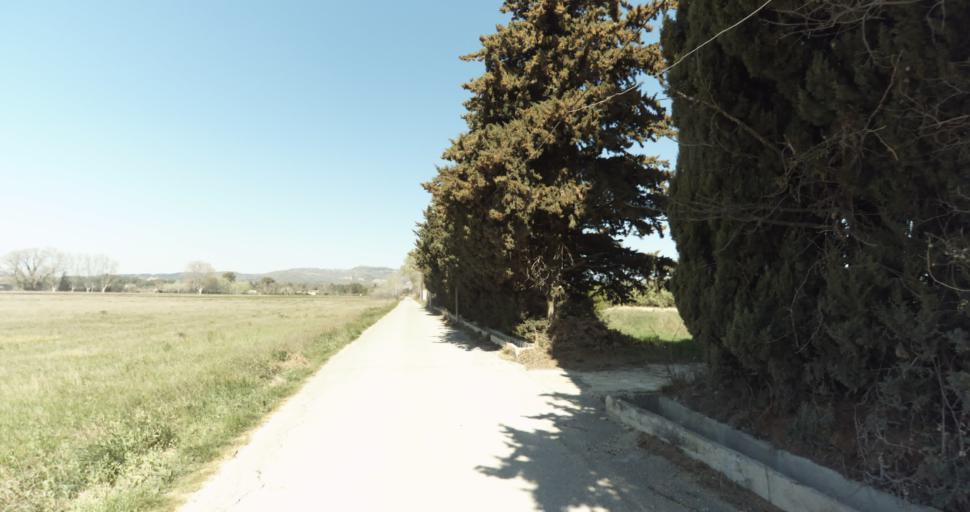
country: FR
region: Provence-Alpes-Cote d'Azur
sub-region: Departement des Bouches-du-Rhone
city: Pelissanne
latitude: 43.6209
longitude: 5.1478
